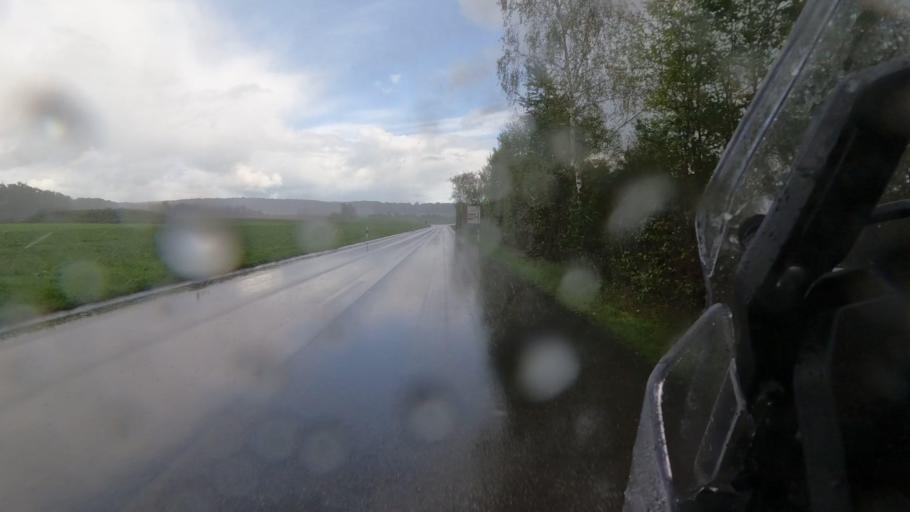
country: CH
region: Zurich
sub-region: Bezirk Andelfingen
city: Dachsen
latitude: 47.6393
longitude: 8.6229
